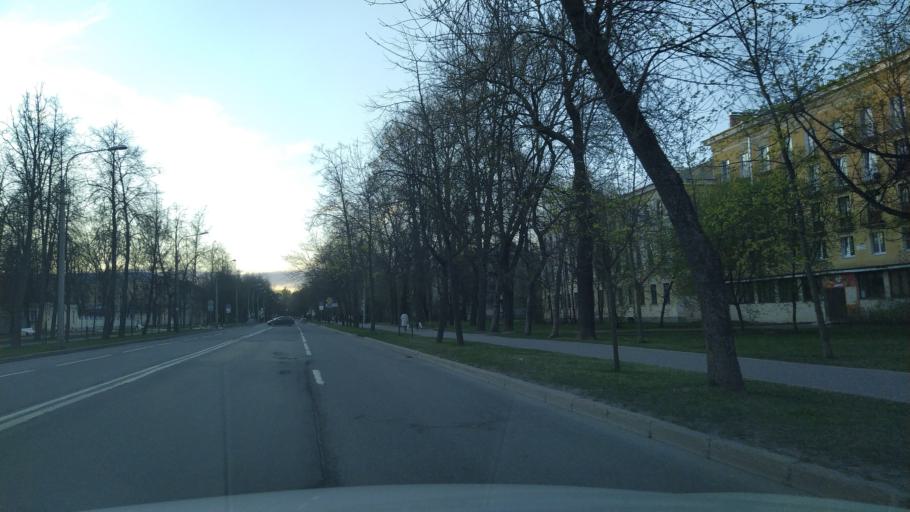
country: RU
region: St.-Petersburg
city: Pushkin
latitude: 59.7061
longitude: 30.4053
